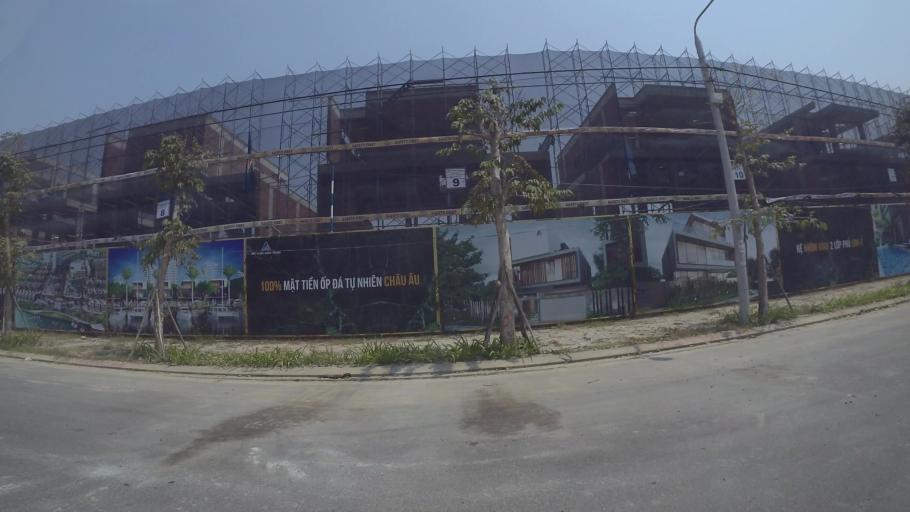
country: VN
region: Da Nang
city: Ngu Hanh Son
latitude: 15.9876
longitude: 108.2634
